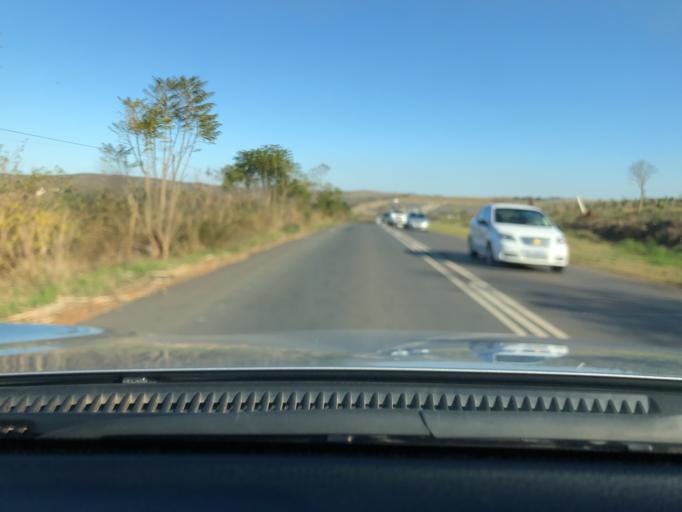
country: ZA
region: KwaZulu-Natal
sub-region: uMgungundlovu District Municipality
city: Camperdown
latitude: -29.7975
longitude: 30.5137
